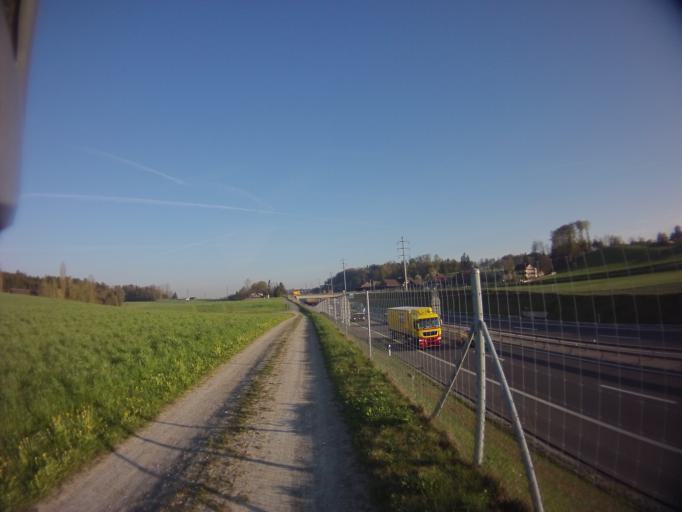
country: CH
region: Zurich
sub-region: Bezirk Affoltern
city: Mettmenstetten
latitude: 47.2486
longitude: 8.4509
